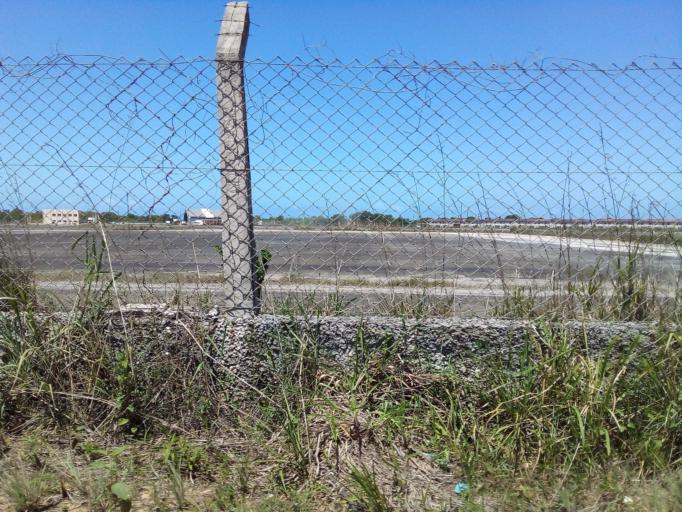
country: BR
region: Espirito Santo
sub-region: Aracruz
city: Aracruz
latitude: -19.8198
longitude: -40.0674
